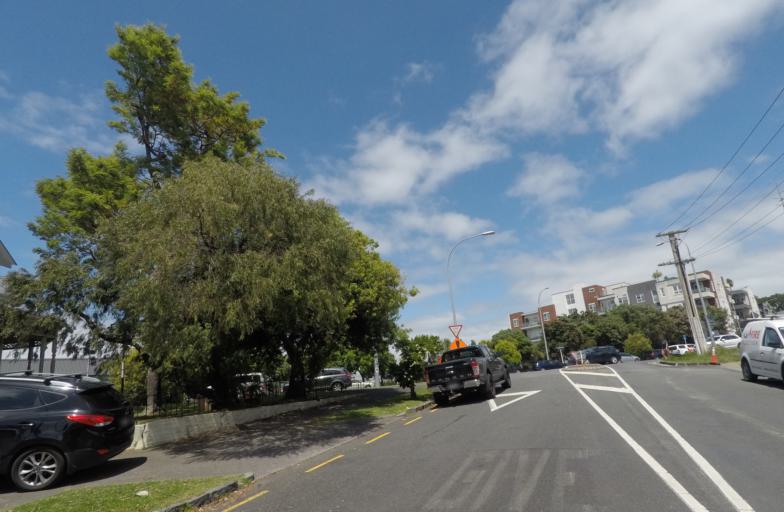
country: NZ
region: Auckland
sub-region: Auckland
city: Auckland
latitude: -36.8622
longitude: 174.7357
